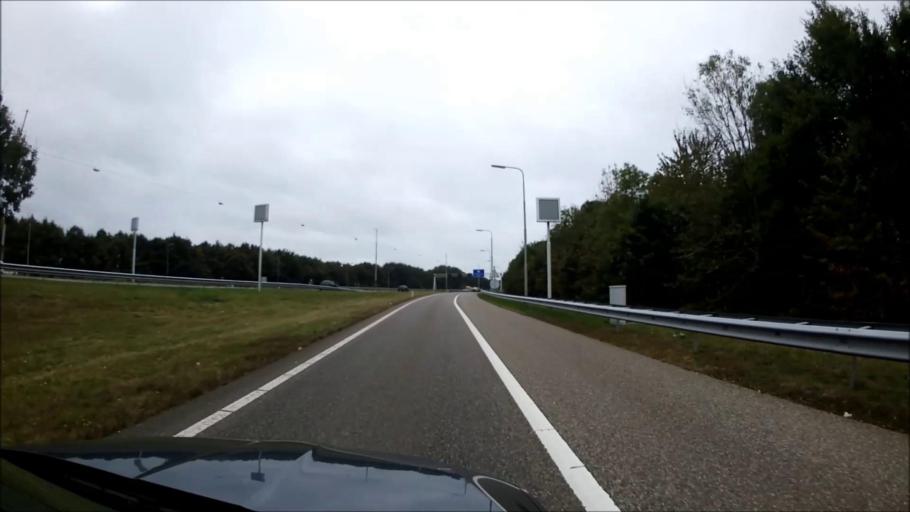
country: NL
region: North Holland
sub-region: Gemeente Naarden
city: Naarden
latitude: 52.3062
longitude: 5.1411
